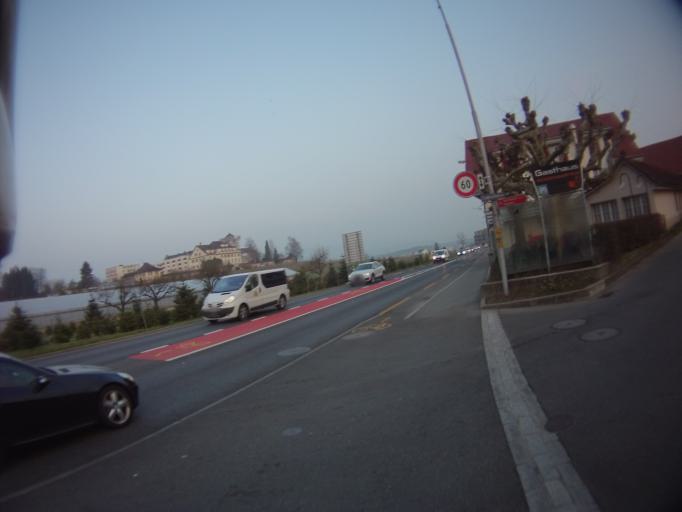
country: CH
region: Zug
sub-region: Zug
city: Cham
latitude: 47.1922
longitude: 8.4455
